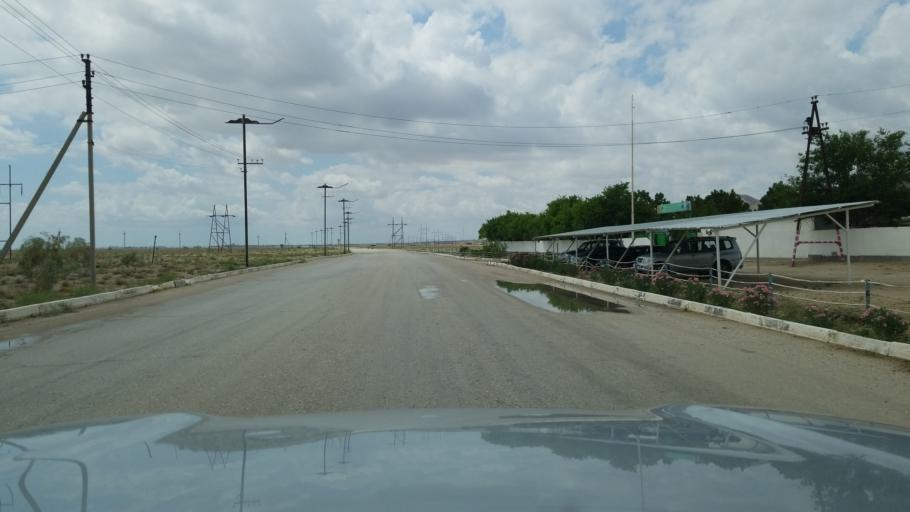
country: TM
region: Balkan
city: Balkanabat
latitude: 39.4795
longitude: 54.4578
